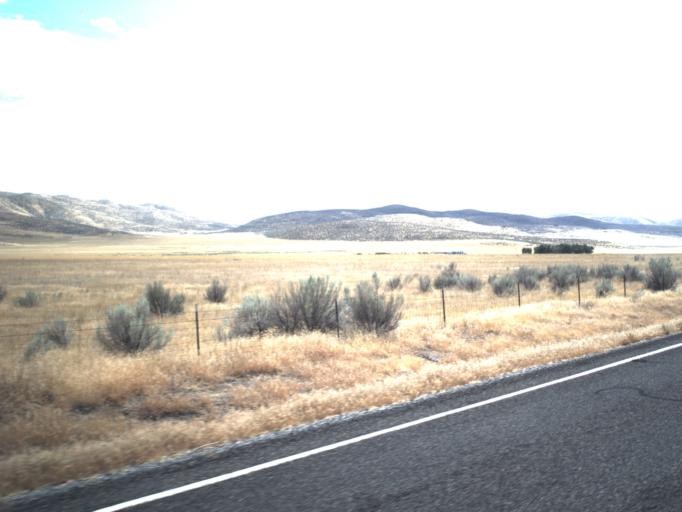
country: US
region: Utah
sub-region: Box Elder County
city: Garland
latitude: 41.8078
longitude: -112.4165
